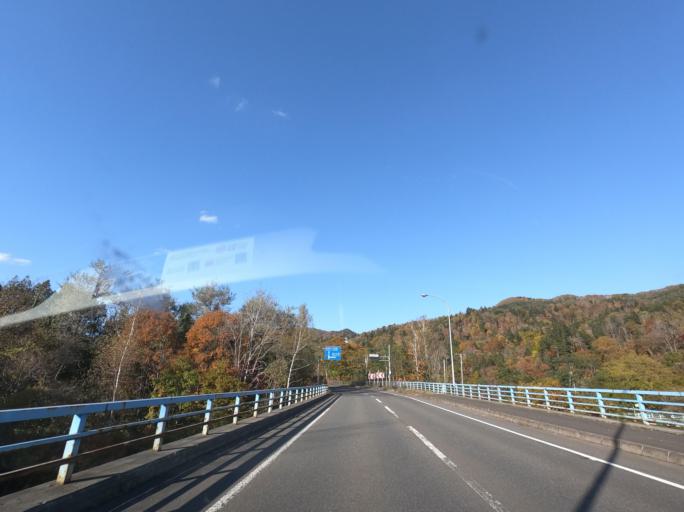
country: JP
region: Hokkaido
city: Iwamizawa
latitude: 43.0048
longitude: 142.0059
